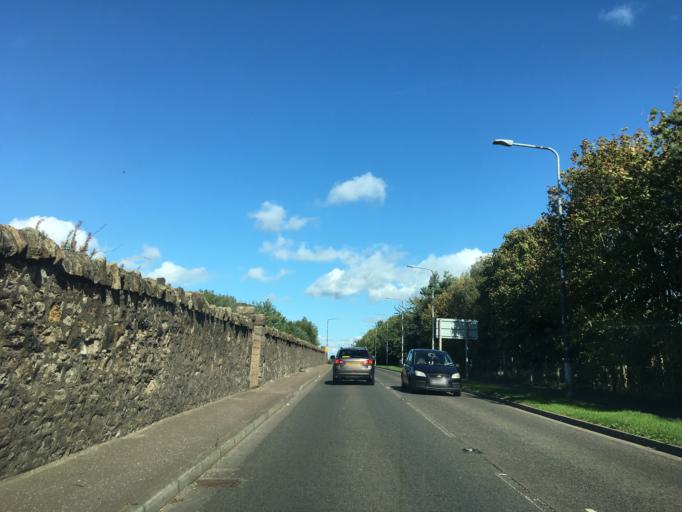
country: GB
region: Scotland
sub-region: Midlothian
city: Bonnyrigg
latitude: 55.9143
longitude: -3.1171
